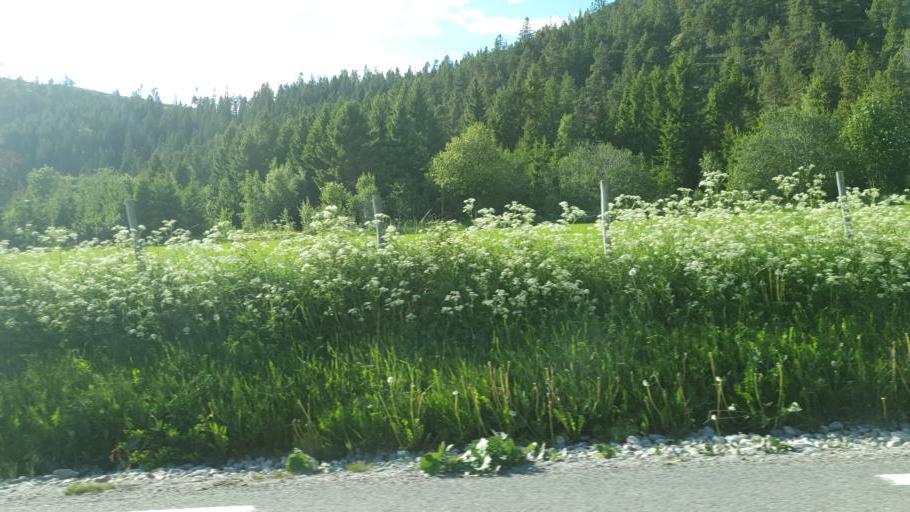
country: NO
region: Sor-Trondelag
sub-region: Skaun
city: Borsa
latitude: 63.5009
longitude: 10.1222
